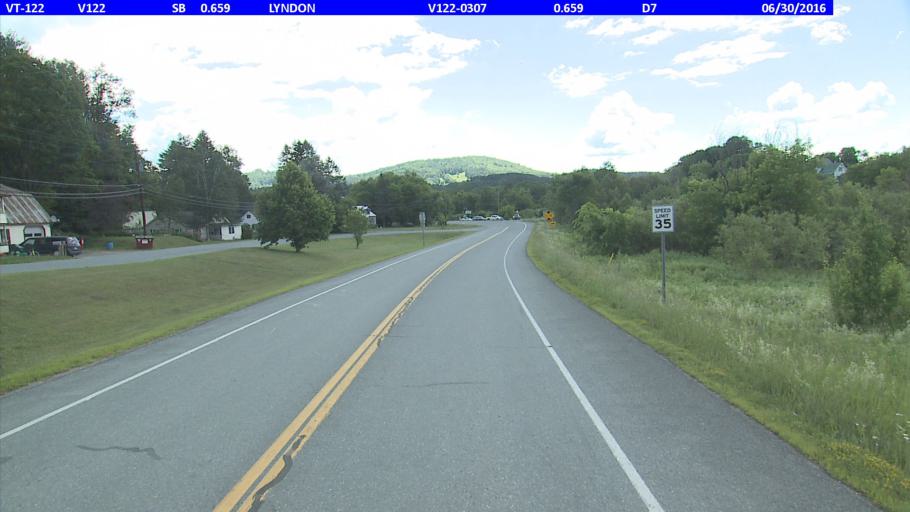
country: US
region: Vermont
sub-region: Caledonia County
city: Lyndonville
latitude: 44.5436
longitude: -72.0119
